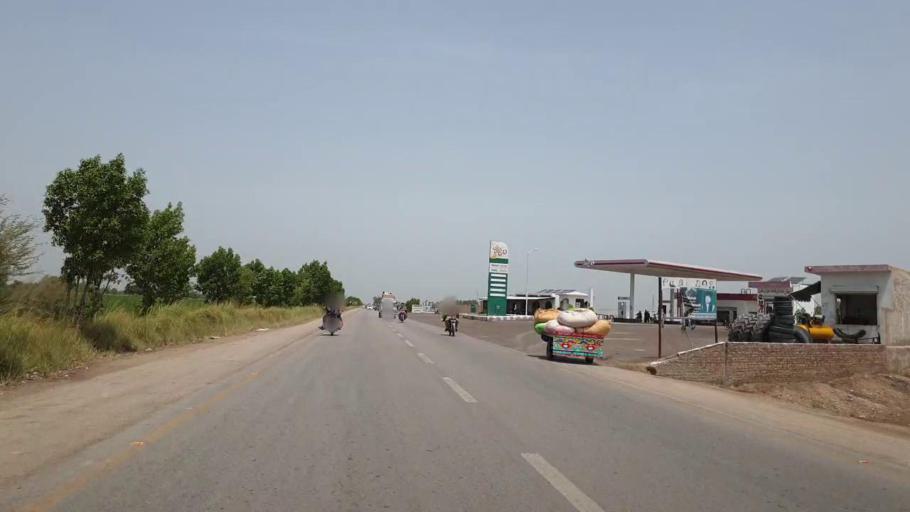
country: PK
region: Sindh
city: Nawabshah
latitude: 26.2233
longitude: 68.4961
